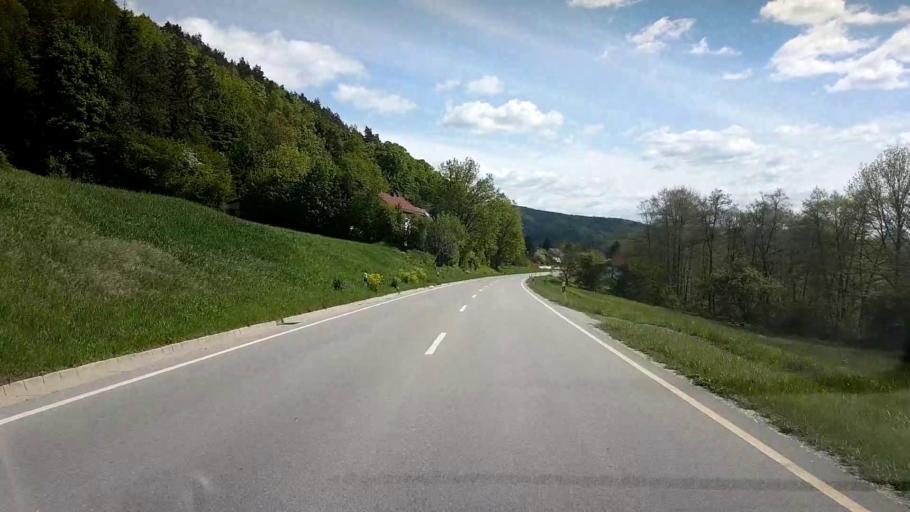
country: DE
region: Bavaria
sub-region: Upper Franconia
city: Ebermannstadt
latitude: 49.7909
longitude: 11.1789
